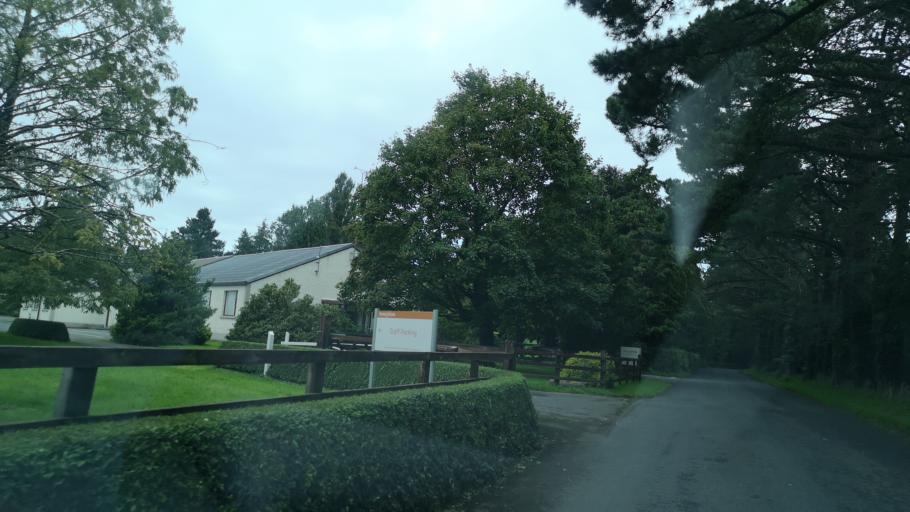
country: IE
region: Leinster
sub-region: Uibh Fhaili
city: Ferbane
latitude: 53.2277
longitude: -7.7297
